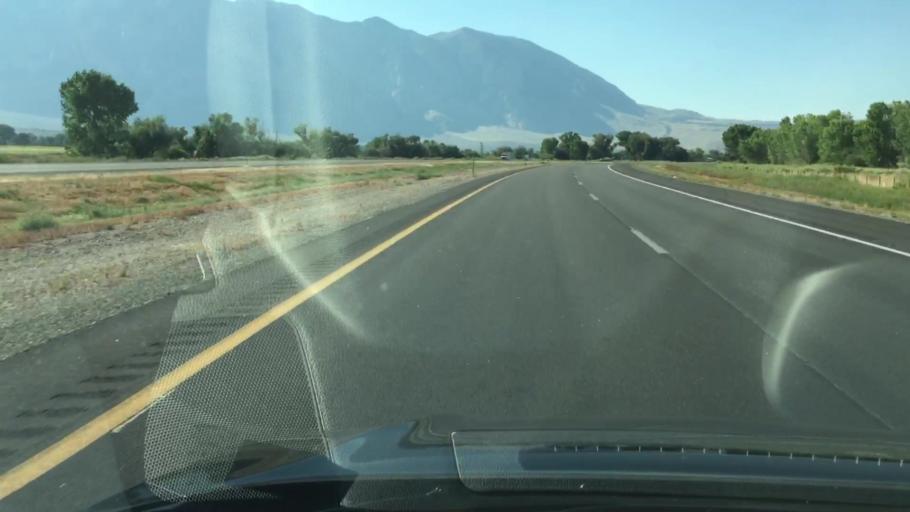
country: US
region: California
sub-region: Inyo County
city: West Bishop
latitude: 37.4086
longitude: -118.5481
